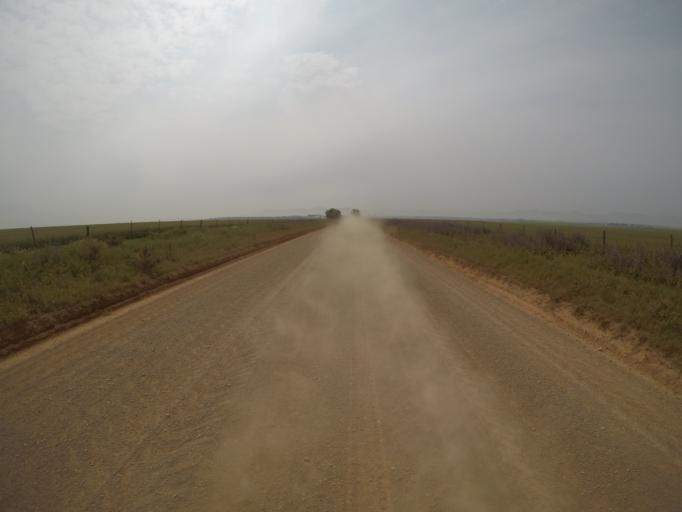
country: ZA
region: Western Cape
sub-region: City of Cape Town
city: Kraaifontein
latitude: -33.7199
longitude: 18.6773
